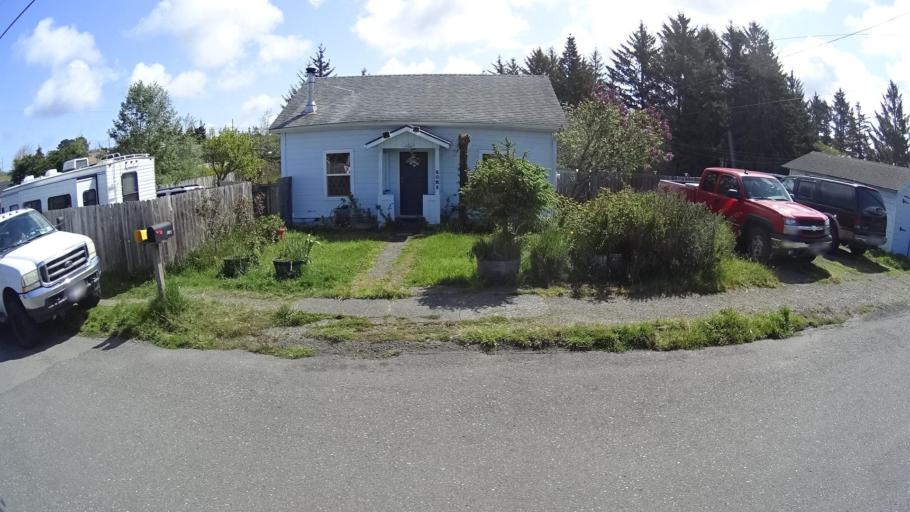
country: US
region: California
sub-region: Humboldt County
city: Bayview
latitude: 40.7611
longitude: -124.1781
